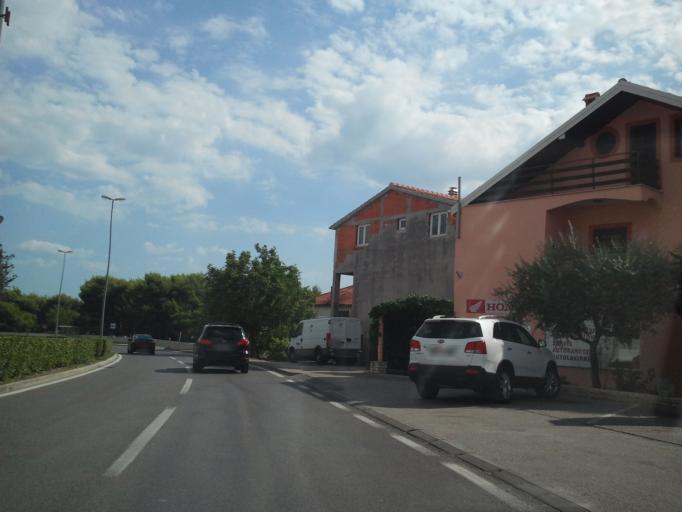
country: HR
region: Zadarska
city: Zadar
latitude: 44.1131
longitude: 15.2543
